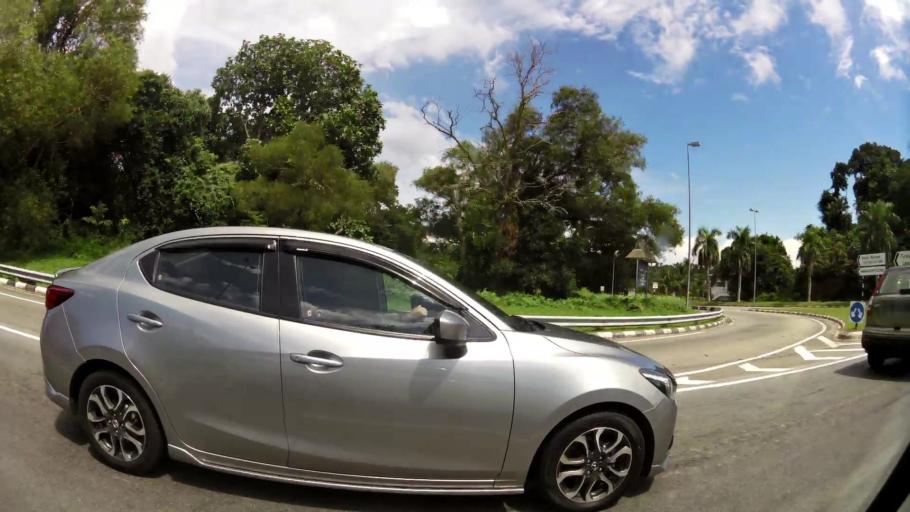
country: BN
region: Brunei and Muara
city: Bandar Seri Begawan
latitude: 4.9818
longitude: 114.9588
